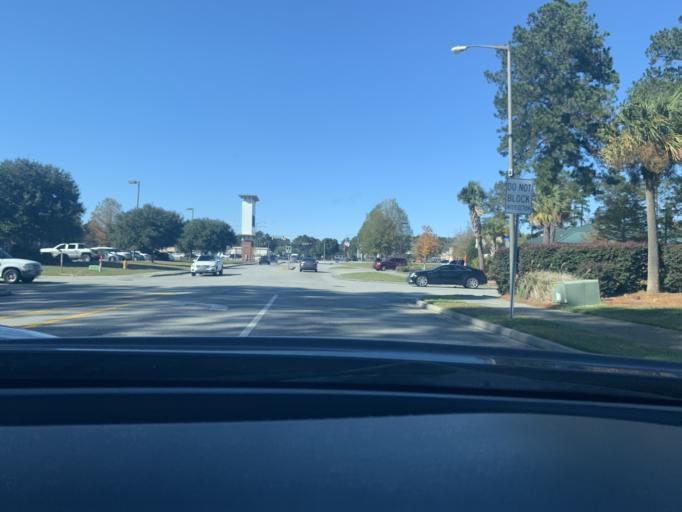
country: US
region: Georgia
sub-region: Chatham County
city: Pooler
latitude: 32.1347
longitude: -81.2527
